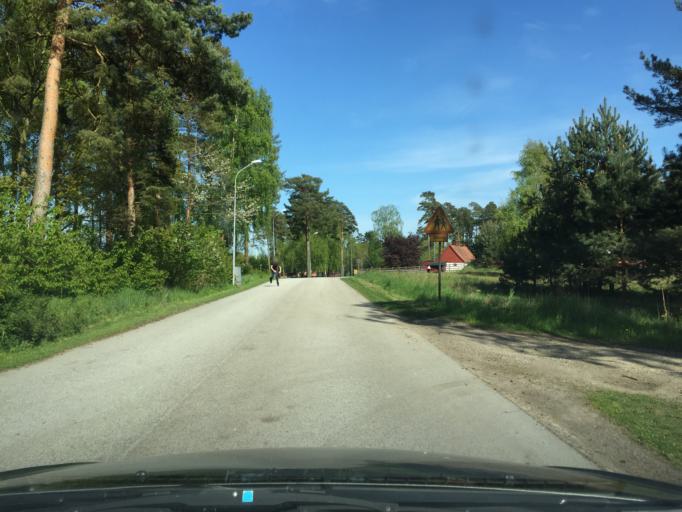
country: SE
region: Skane
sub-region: Sjobo Kommun
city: Blentarp
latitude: 55.5821
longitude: 13.5966
